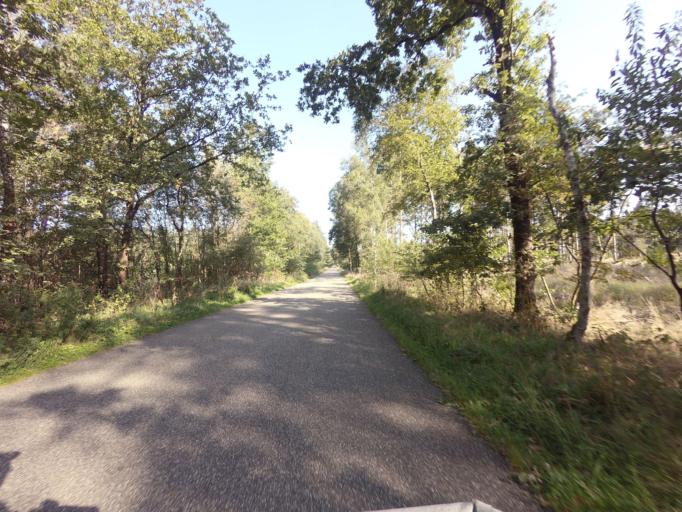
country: DE
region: Lower Saxony
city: Wielen
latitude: 52.5298
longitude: 6.7280
